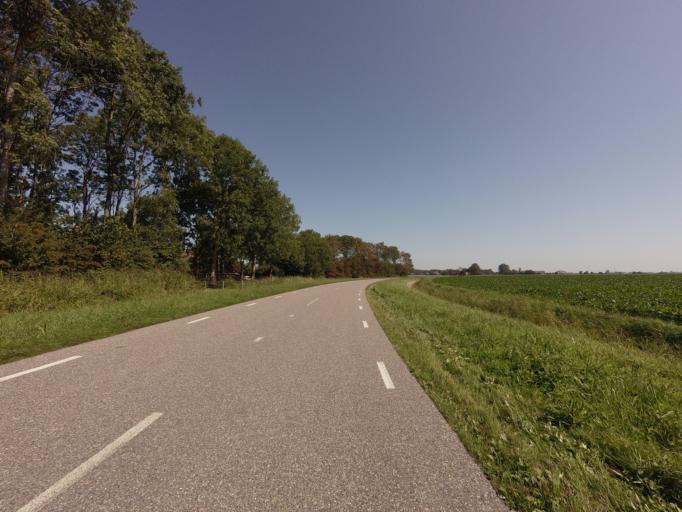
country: NL
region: Friesland
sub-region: Gemeente Dongeradeel
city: Ternaard
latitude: 53.3672
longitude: 5.9825
